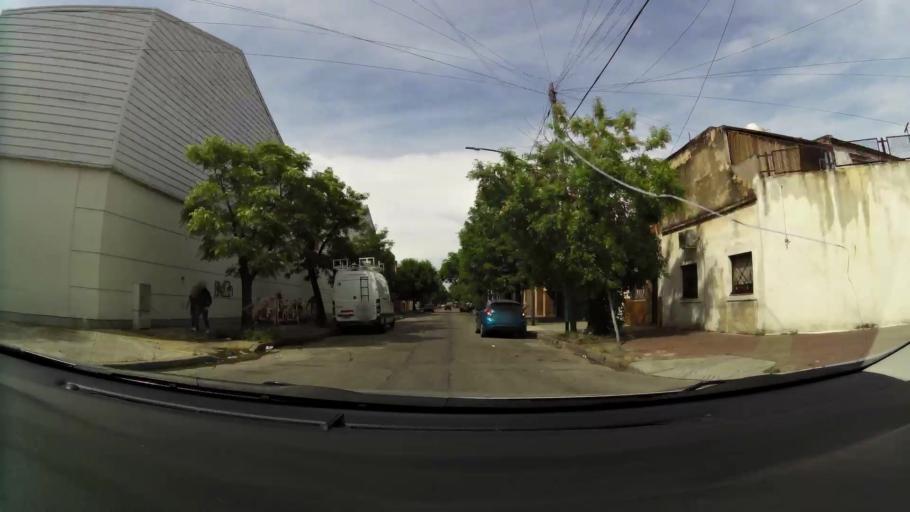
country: AR
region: Buenos Aires F.D.
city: Villa Lugano
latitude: -34.6553
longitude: -58.4350
